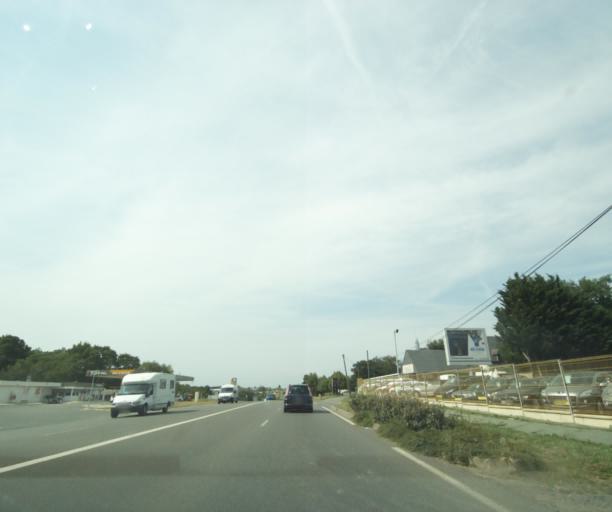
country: FR
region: Centre
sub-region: Departement d'Indre-et-Loire
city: Chambray-les-Tours
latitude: 47.3157
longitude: 0.7114
